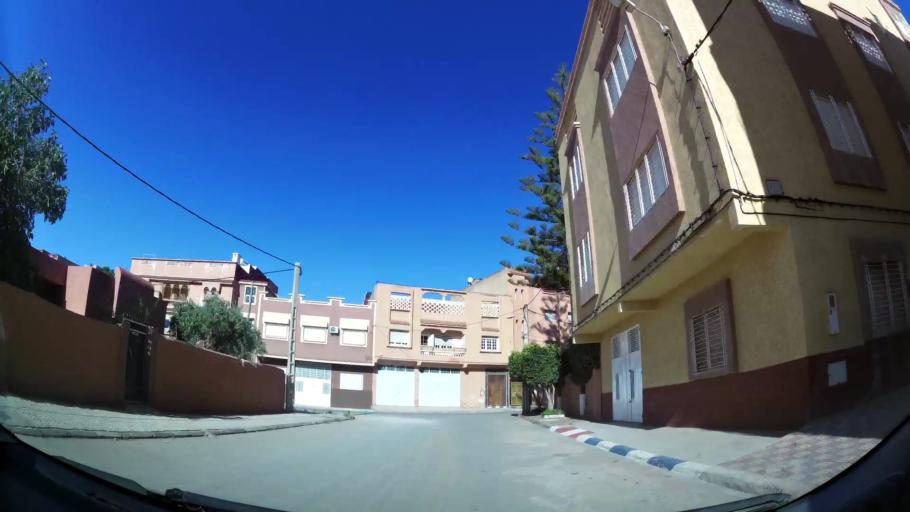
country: MA
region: Oriental
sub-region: Berkane-Taourirt
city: Berkane
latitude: 34.9326
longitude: -2.3294
